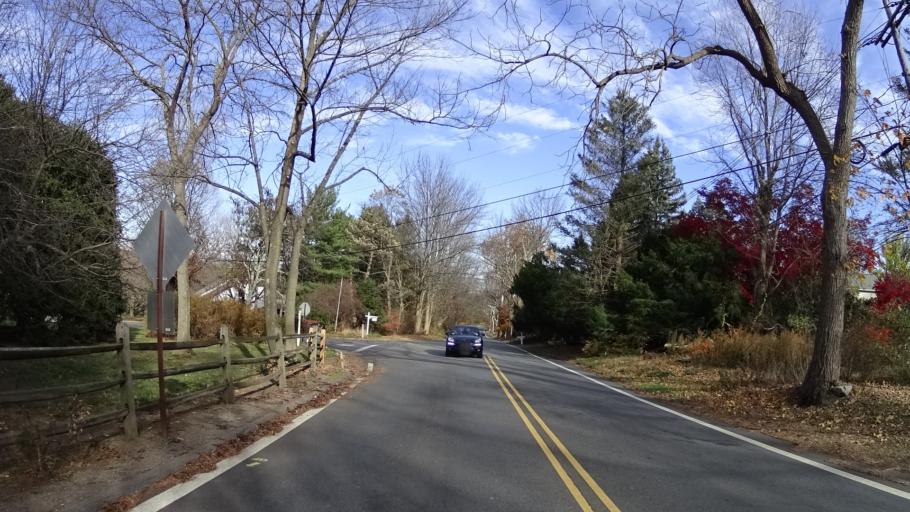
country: US
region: New Jersey
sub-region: Morris County
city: Mendham
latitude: 40.7850
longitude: -74.5735
